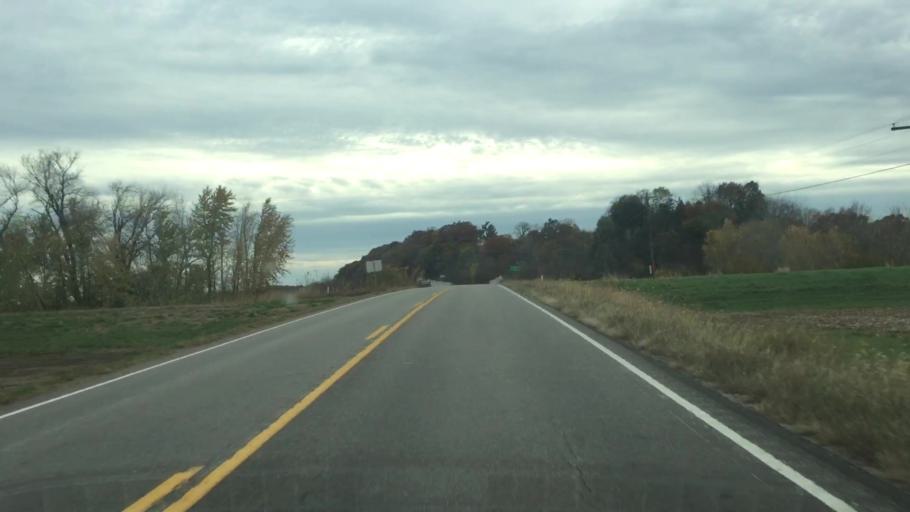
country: US
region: Missouri
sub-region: Callaway County
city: Fulton
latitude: 38.6978
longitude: -91.8262
